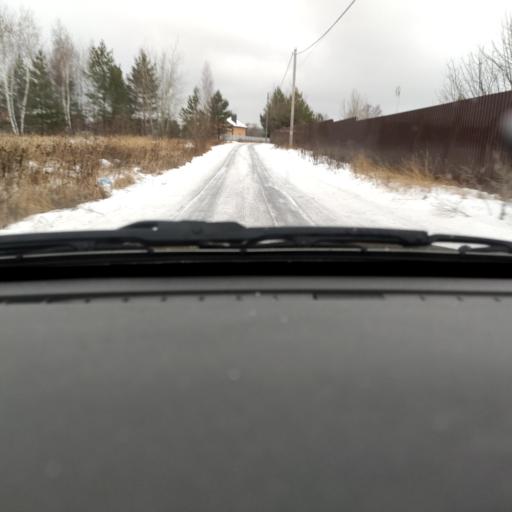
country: RU
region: Voronezj
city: Ramon'
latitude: 51.8945
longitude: 39.2568
